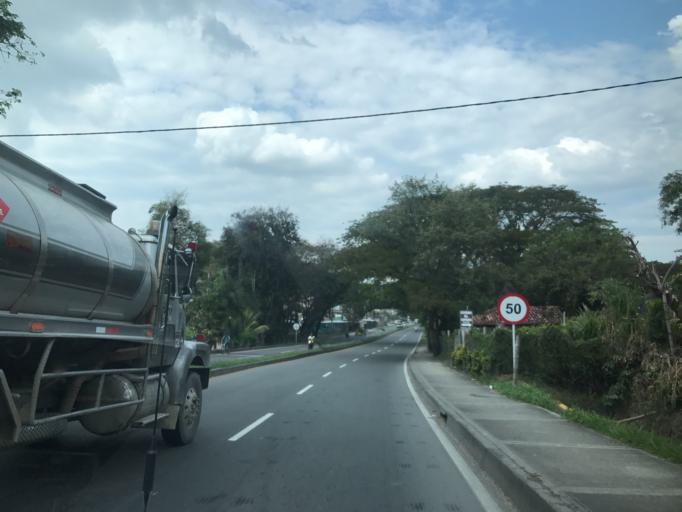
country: CO
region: Valle del Cauca
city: Cartago
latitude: 4.7405
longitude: -75.9027
